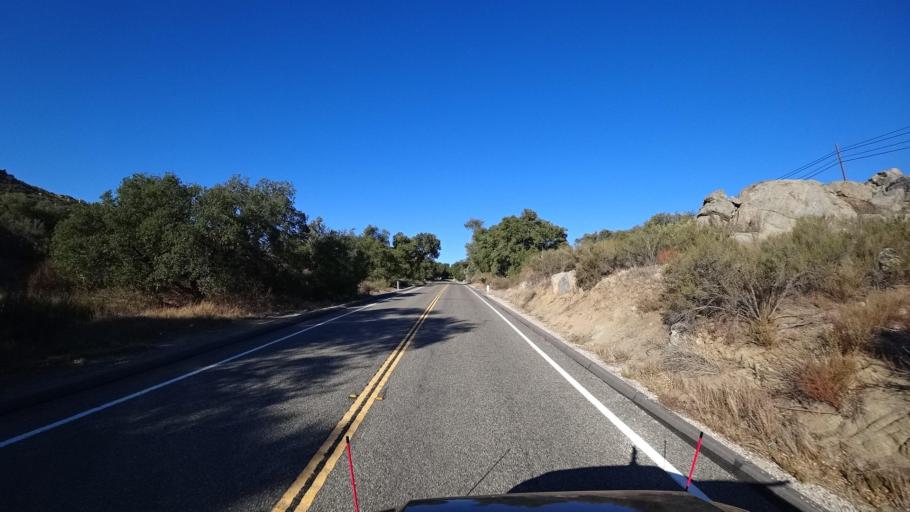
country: MX
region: Baja California
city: Tecate
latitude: 32.5996
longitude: -116.5759
